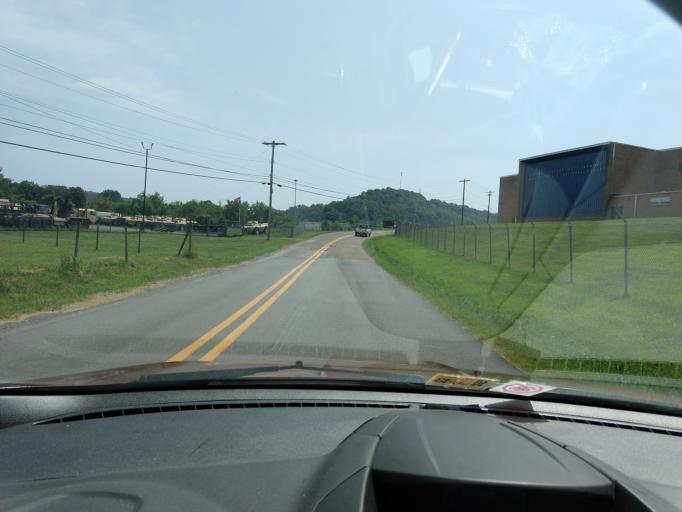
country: US
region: West Virginia
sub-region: Harrison County
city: Clarksburg
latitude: 39.2696
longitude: -80.3682
